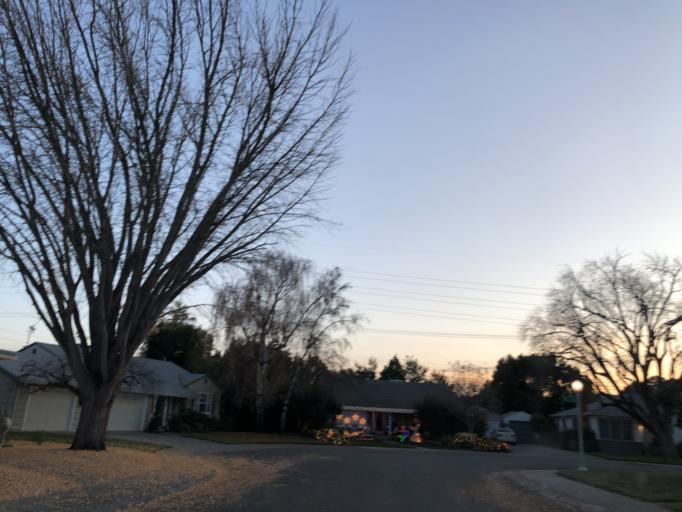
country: US
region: California
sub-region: Sacramento County
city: Sacramento
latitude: 38.5569
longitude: -121.4401
